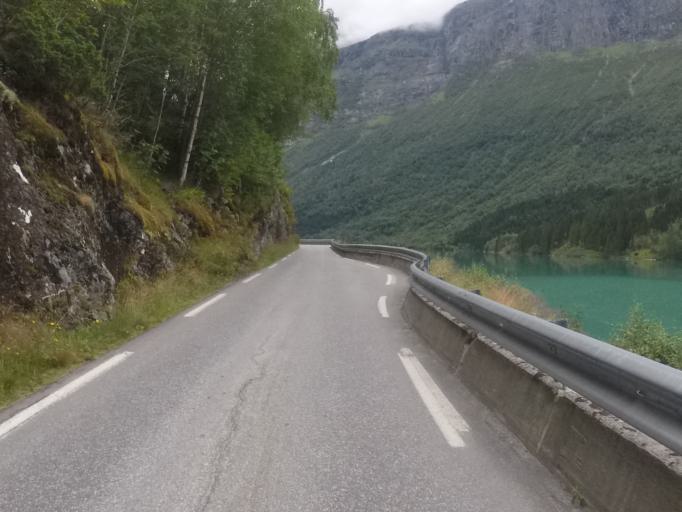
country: NO
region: Sogn og Fjordane
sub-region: Stryn
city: Stryn
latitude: 61.8562
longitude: 6.8956
